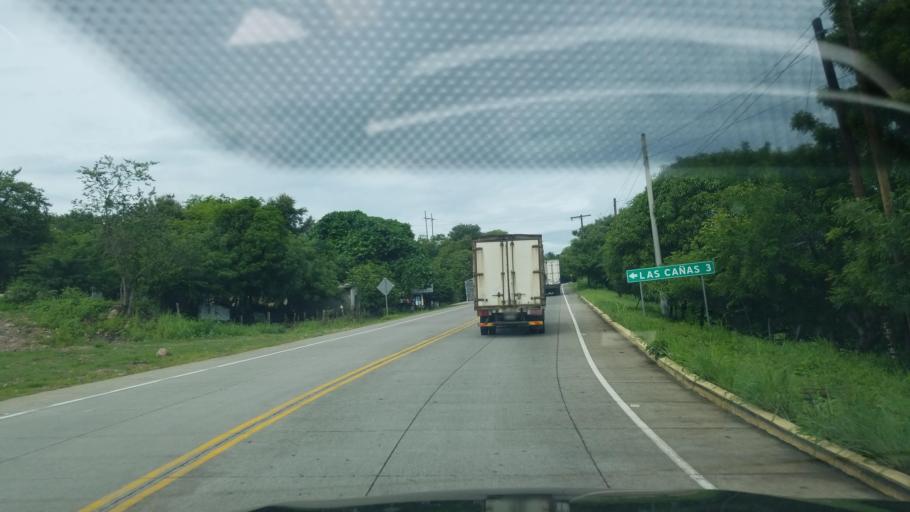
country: HN
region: Francisco Morazan
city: El Porvenir
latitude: 13.6783
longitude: -87.3534
